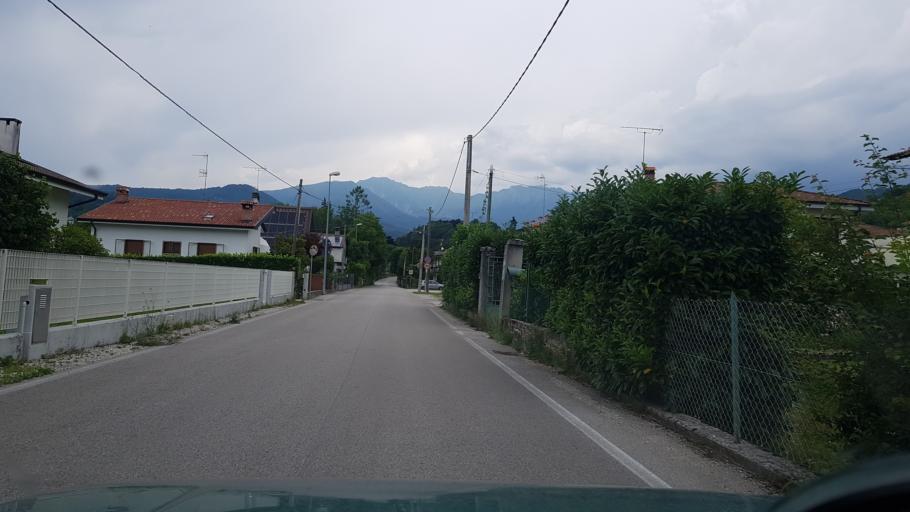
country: IT
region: Friuli Venezia Giulia
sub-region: Provincia di Udine
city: Tarcento
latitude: 46.2117
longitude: 13.2281
